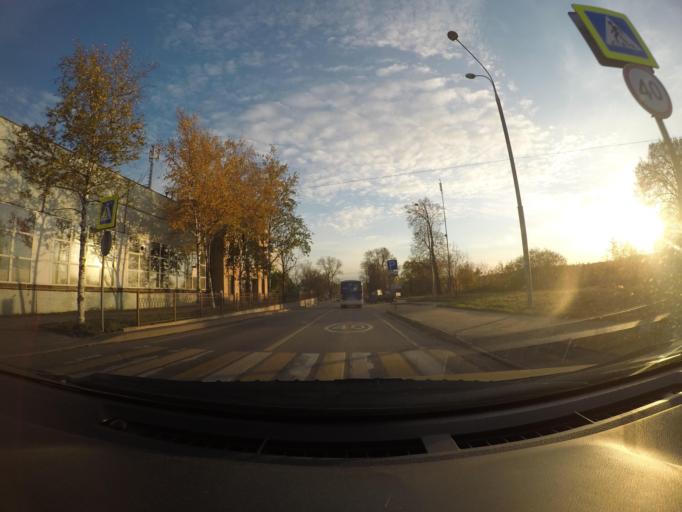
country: RU
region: Moskovskaya
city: Rzhavki
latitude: 55.9760
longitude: 37.2633
